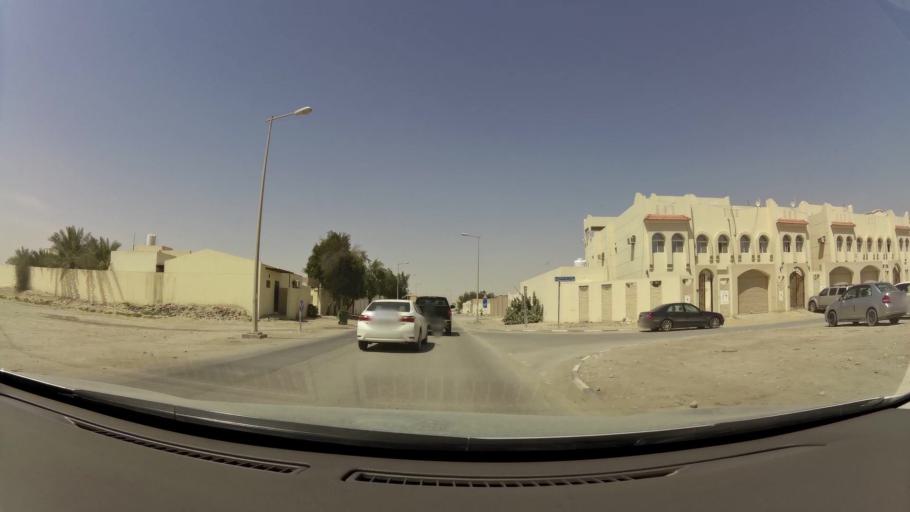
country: QA
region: Baladiyat ar Rayyan
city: Ar Rayyan
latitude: 25.2629
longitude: 51.4112
